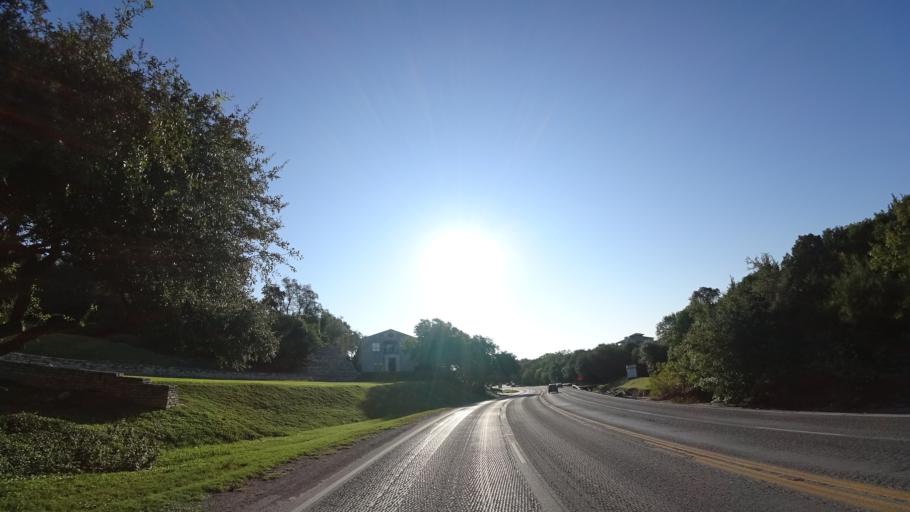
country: US
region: Texas
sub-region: Travis County
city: Rollingwood
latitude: 30.2716
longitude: -97.7947
